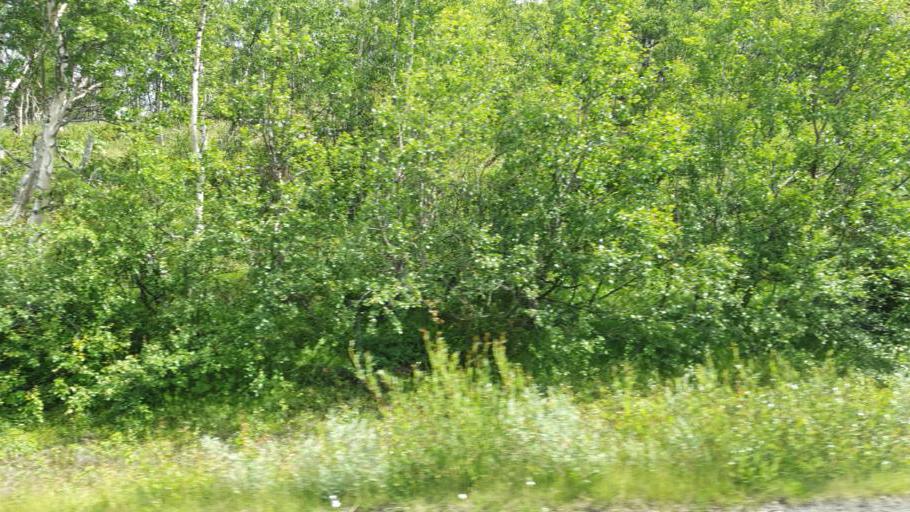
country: NO
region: Oppland
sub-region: Lom
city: Fossbergom
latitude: 61.4916
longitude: 8.8171
